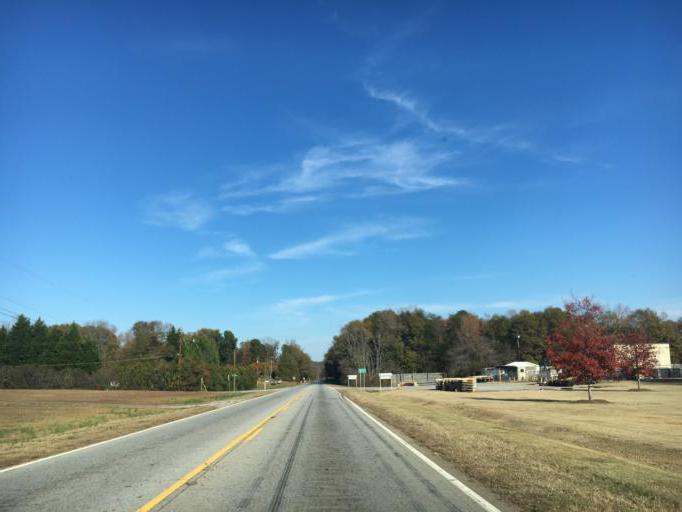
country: US
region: South Carolina
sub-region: Spartanburg County
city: Lyman
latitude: 34.9601
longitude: -82.1209
